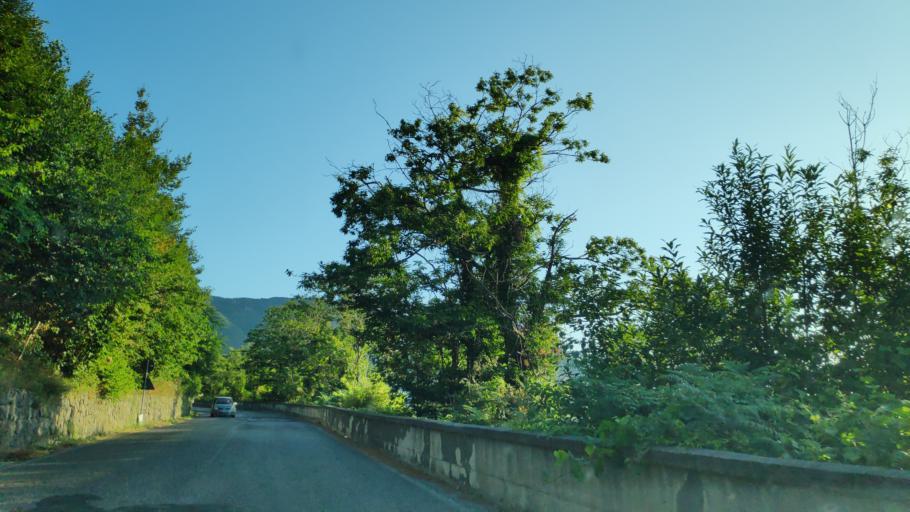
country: IT
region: Campania
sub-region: Provincia di Salerno
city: Corbara
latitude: 40.7212
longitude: 14.6047
